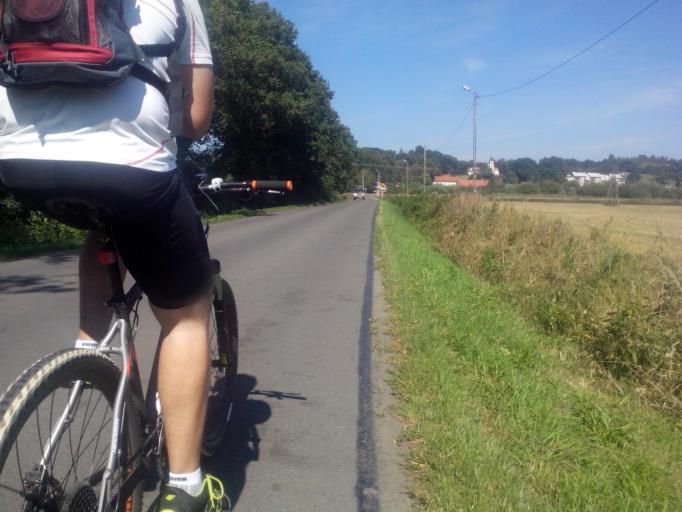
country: PL
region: Subcarpathian Voivodeship
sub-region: Powiat strzyzowski
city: Wisniowa
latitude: 49.8624
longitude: 21.6480
